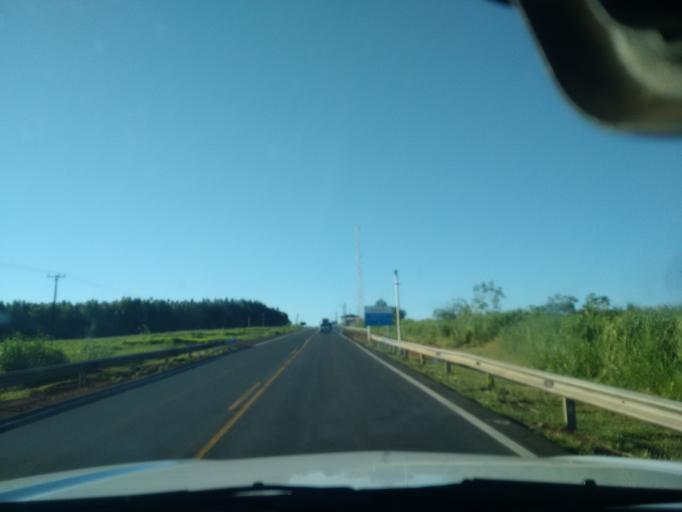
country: BR
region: Mato Grosso do Sul
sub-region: Eldorado
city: Eldorado
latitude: -23.8715
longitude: -54.3255
